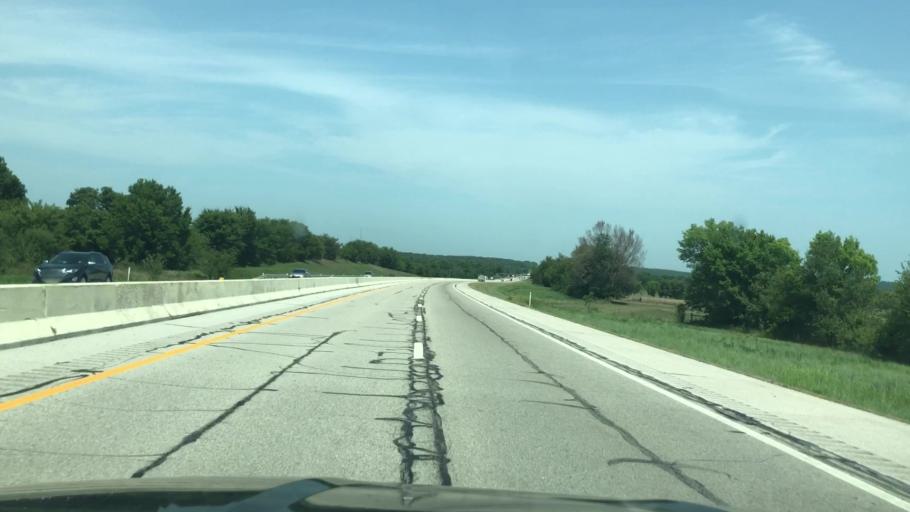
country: US
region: Oklahoma
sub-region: Rogers County
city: Chelsea
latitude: 36.4456
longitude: -95.3739
